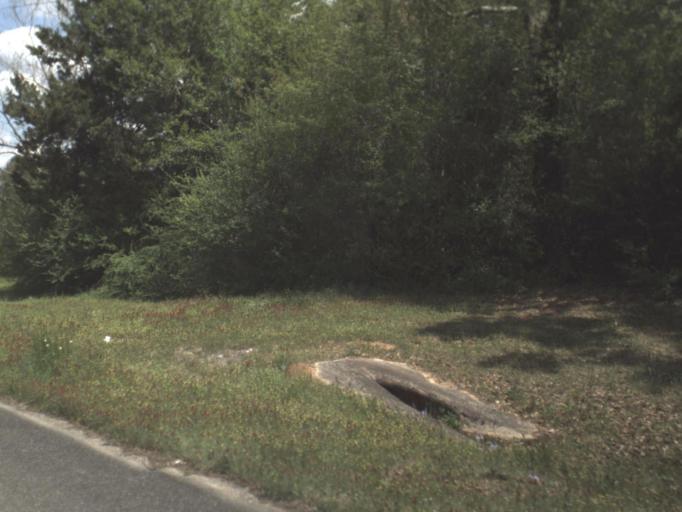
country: US
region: Florida
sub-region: Okaloosa County
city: Crestview
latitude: 30.9888
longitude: -86.6293
